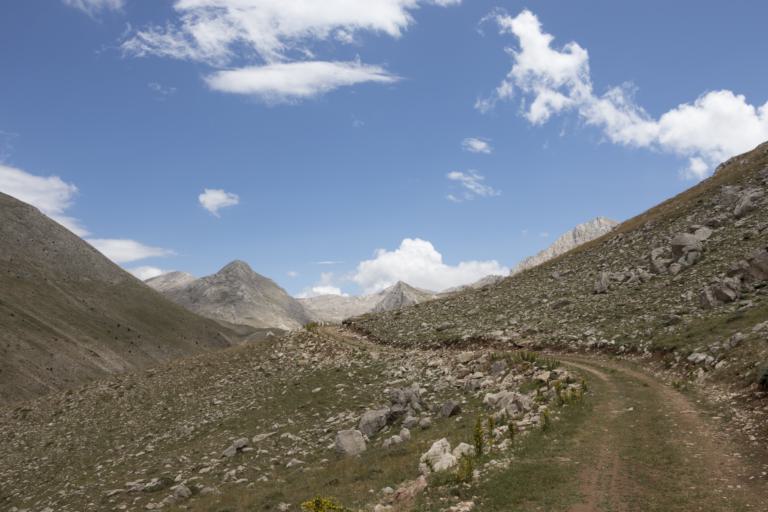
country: TR
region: Adana
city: Tufanbeyli
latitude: 38.4246
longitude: 36.1850
